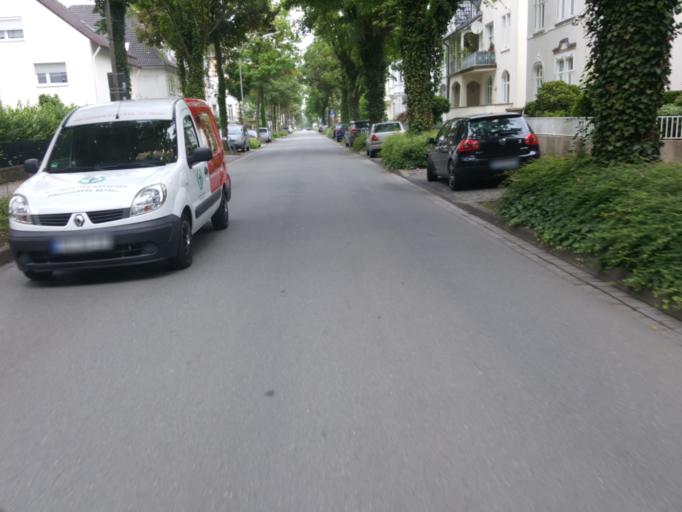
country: DE
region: North Rhine-Westphalia
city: Bad Oeynhausen
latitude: 52.1996
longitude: 8.8009
